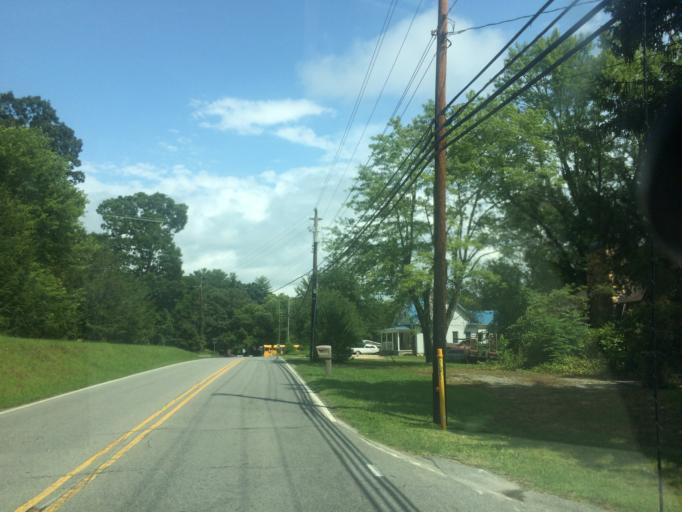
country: US
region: North Carolina
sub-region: Henderson County
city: Laurel Park
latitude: 35.3199
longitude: -82.4839
